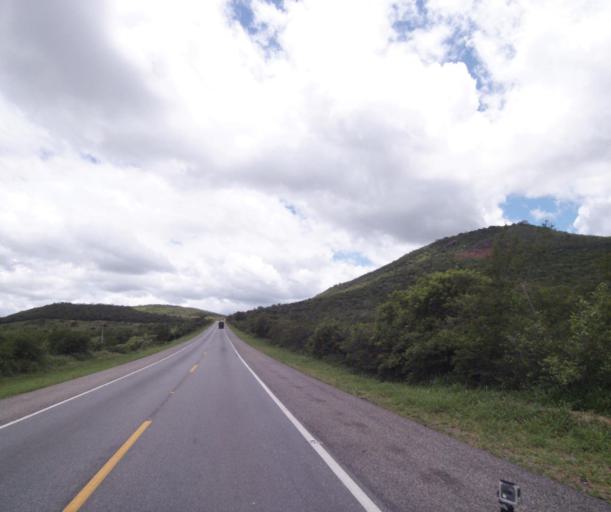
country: BR
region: Bahia
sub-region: Pocoes
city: Pocoes
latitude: -14.3731
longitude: -40.3467
